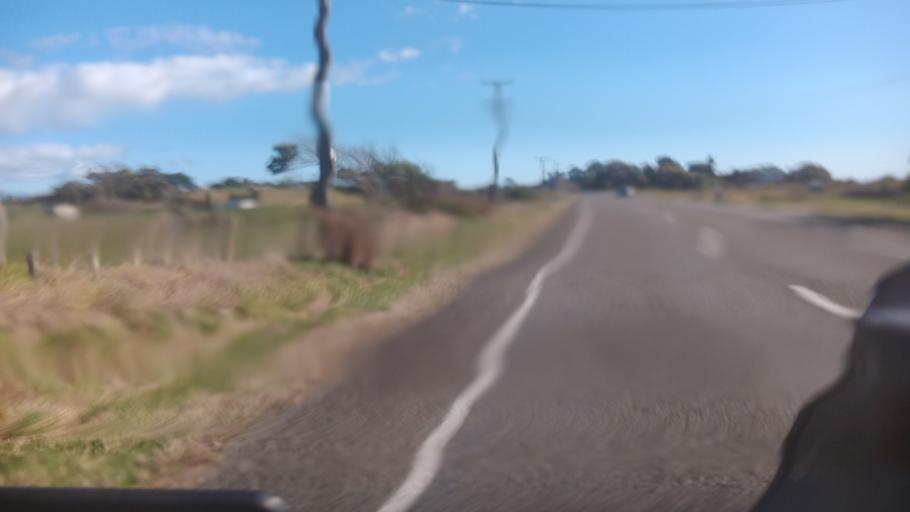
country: NZ
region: Bay of Plenty
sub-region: Opotiki District
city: Opotiki
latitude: -37.9876
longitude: 177.3592
